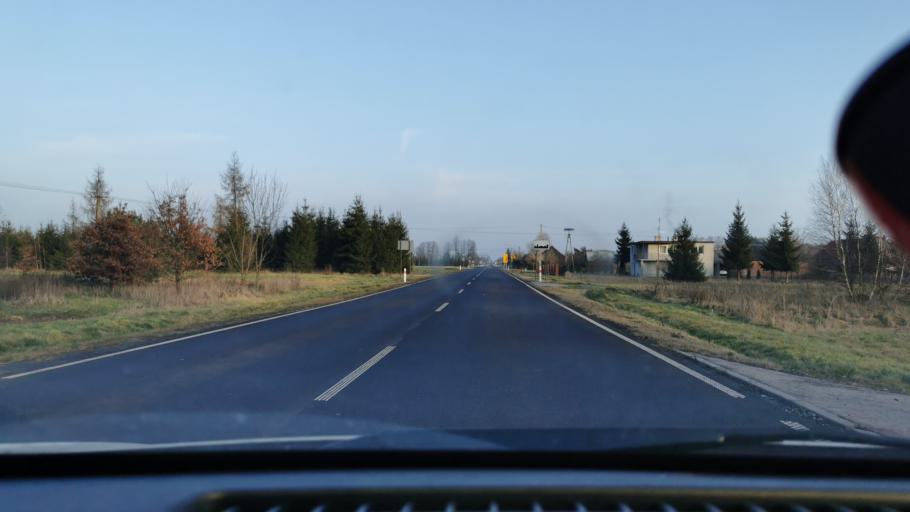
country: PL
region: Lodz Voivodeship
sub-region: Powiat belchatowski
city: Druzbice
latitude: 51.5108
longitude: 19.3672
